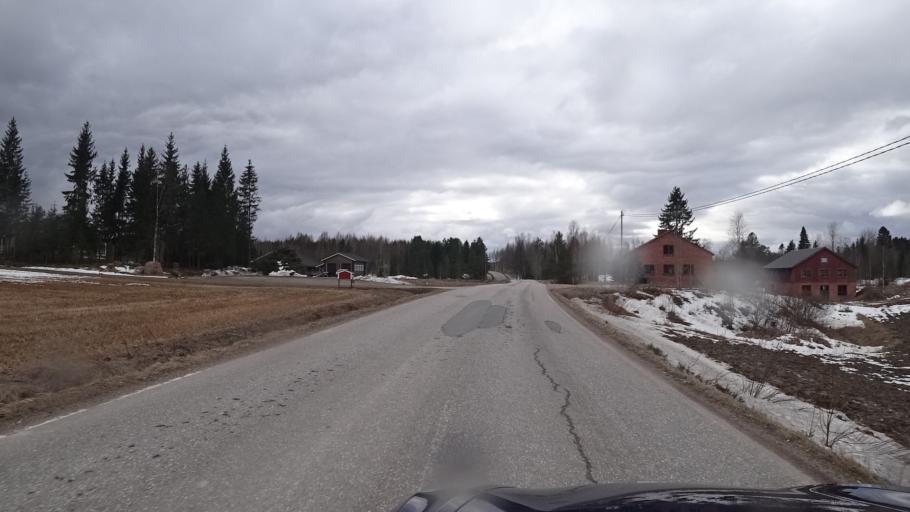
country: FI
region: Paijanne Tavastia
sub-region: Lahti
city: Nastola
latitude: 60.8934
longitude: 26.0115
